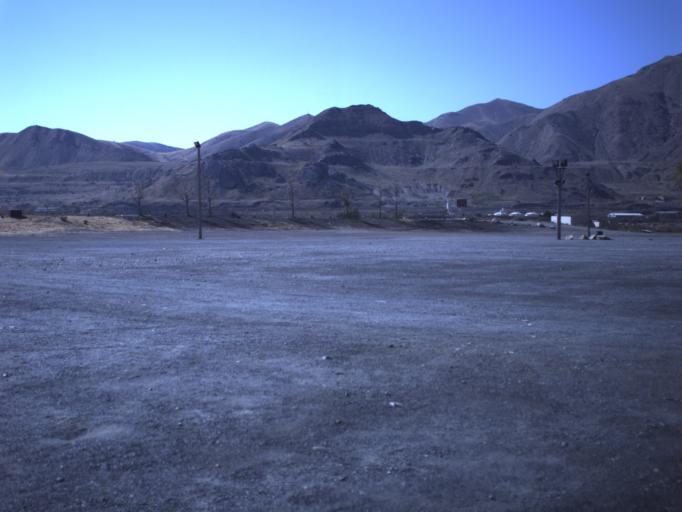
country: US
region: Utah
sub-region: Salt Lake County
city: Magna
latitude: 40.7478
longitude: -112.1869
